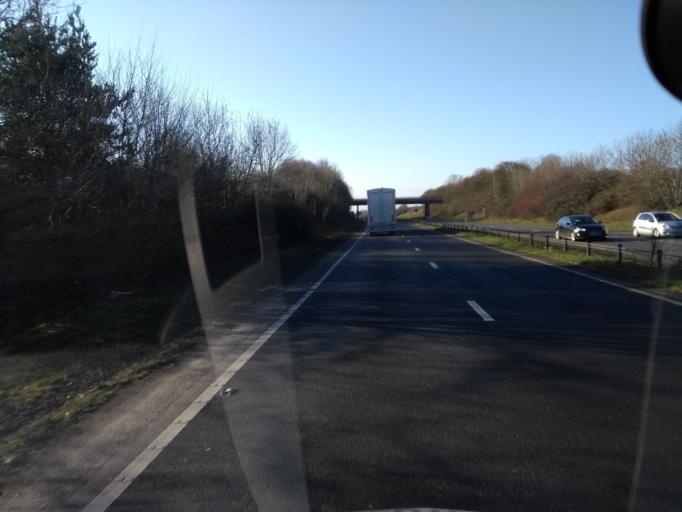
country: GB
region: England
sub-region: Somerset
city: Ilchester
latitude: 51.0156
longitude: -2.6825
